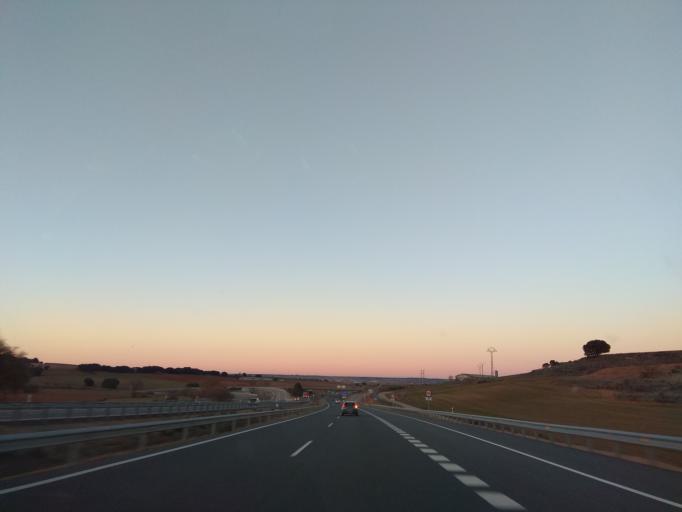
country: ES
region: Castille and Leon
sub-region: Provincia de Burgos
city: Quintanilla de la Mata
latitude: 41.9920
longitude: -3.7622
